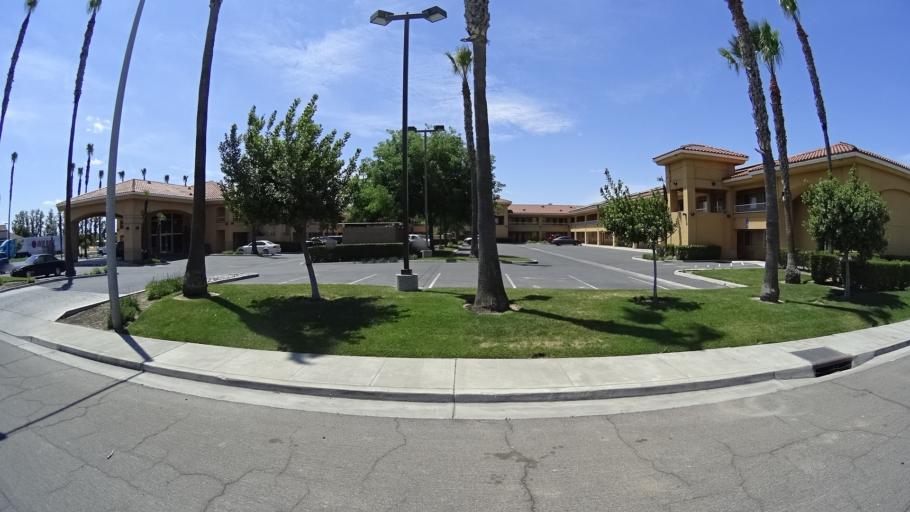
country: US
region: California
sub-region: Kings County
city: Lemoore
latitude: 36.3006
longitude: -119.7694
